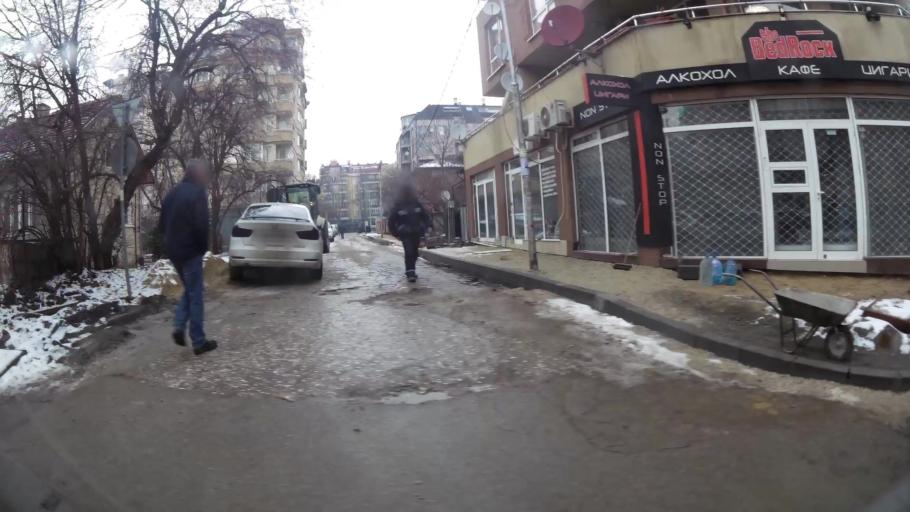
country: BG
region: Sofia-Capital
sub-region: Stolichna Obshtina
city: Sofia
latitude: 42.6789
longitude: 23.2874
